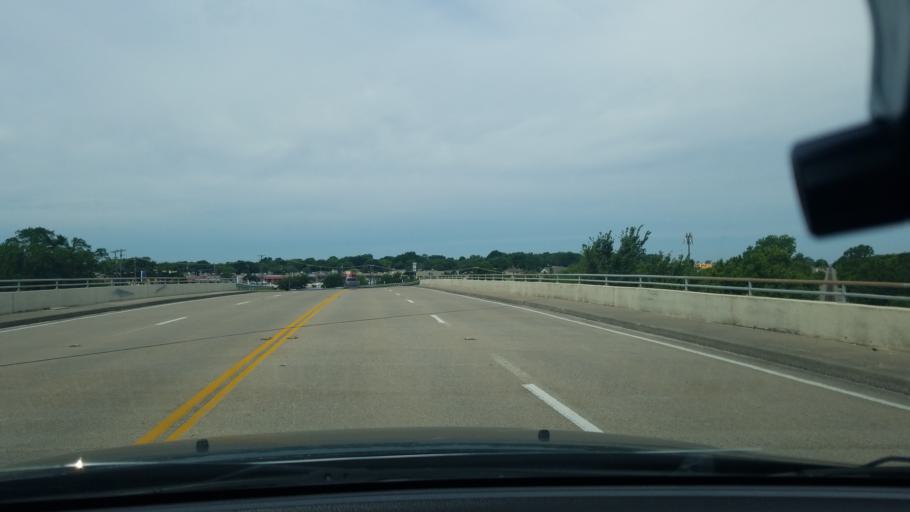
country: US
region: Texas
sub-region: Dallas County
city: Mesquite
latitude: 32.7657
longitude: -96.5802
